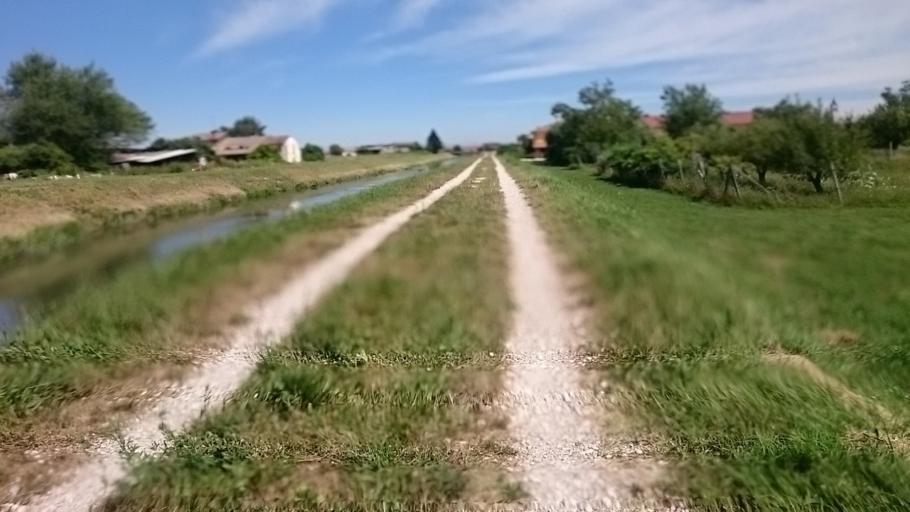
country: IT
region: Veneto
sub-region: Provincia di Padova
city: Pionca
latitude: 45.4632
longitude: 11.9585
